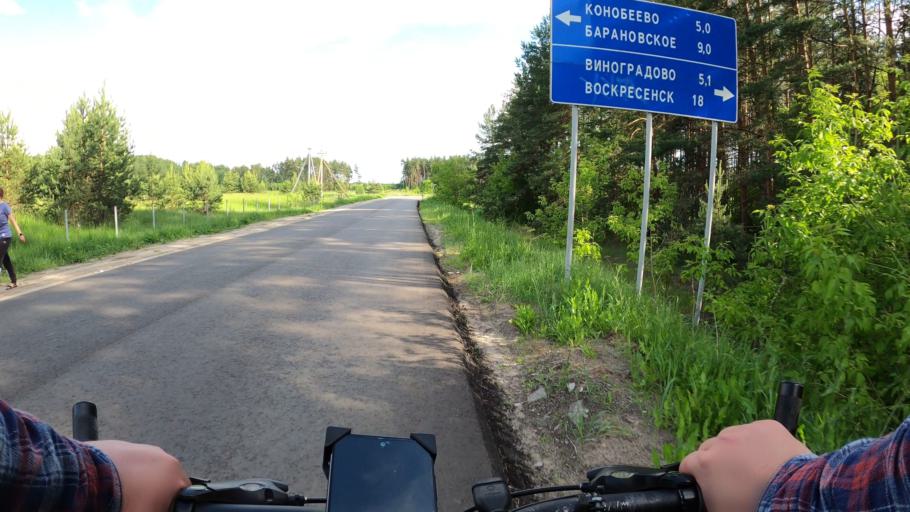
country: RU
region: Moskovskaya
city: Konobeyevo
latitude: 55.4367
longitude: 38.6335
